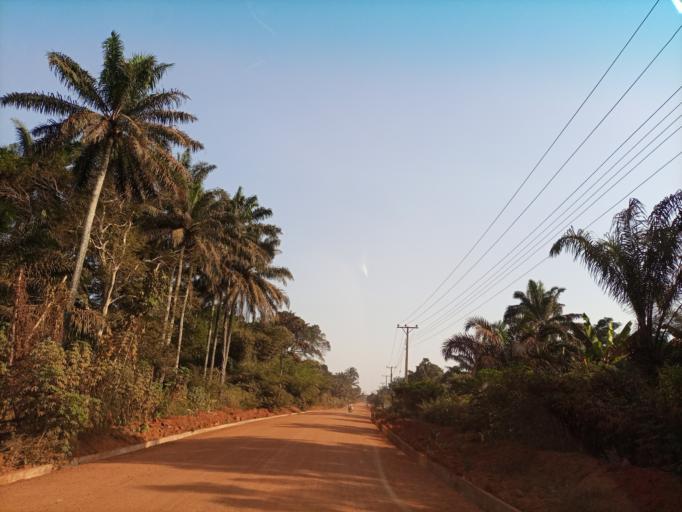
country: NG
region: Enugu
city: Opi
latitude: 6.7529
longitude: 7.4072
